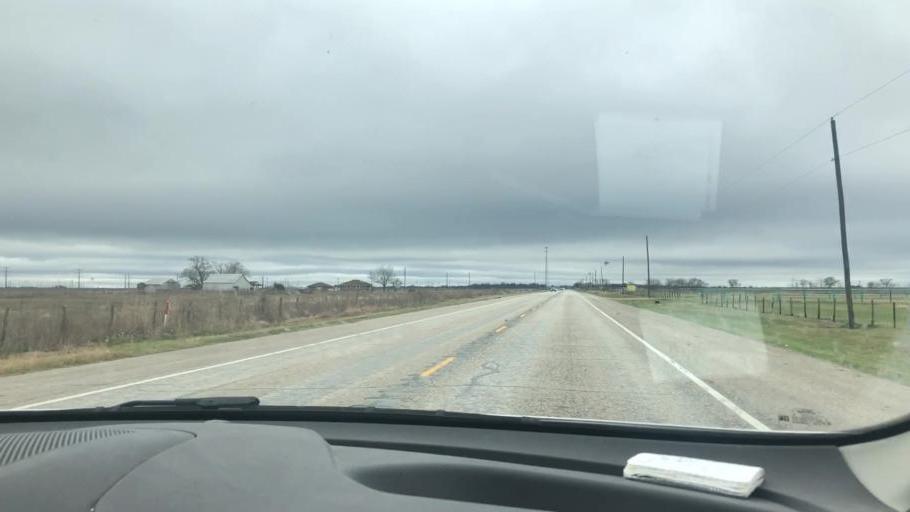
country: US
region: Texas
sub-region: Wharton County
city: Wharton
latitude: 29.2411
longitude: -96.0423
